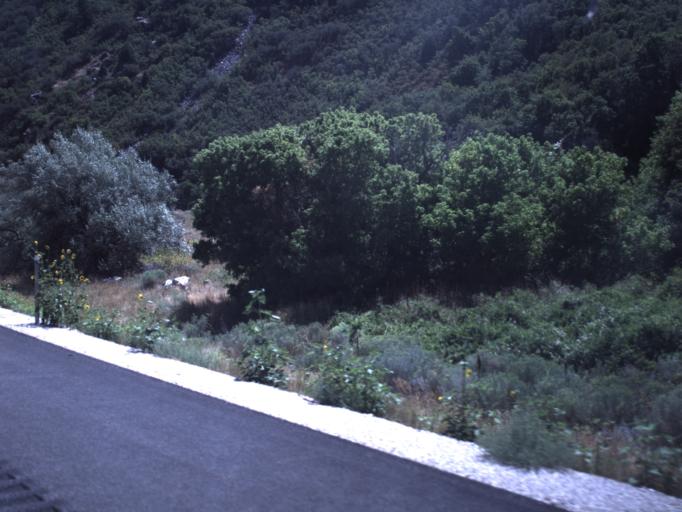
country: US
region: Utah
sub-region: Weber County
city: Uintah
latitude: 41.1379
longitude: -111.8676
